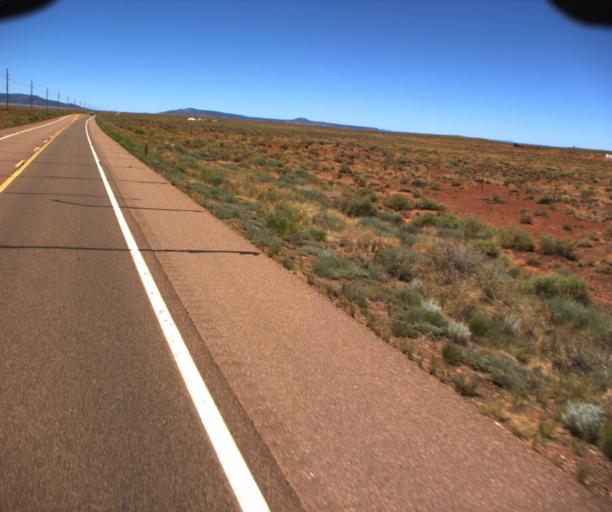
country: US
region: Arizona
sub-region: Coconino County
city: LeChee
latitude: 34.9644
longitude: -110.7378
